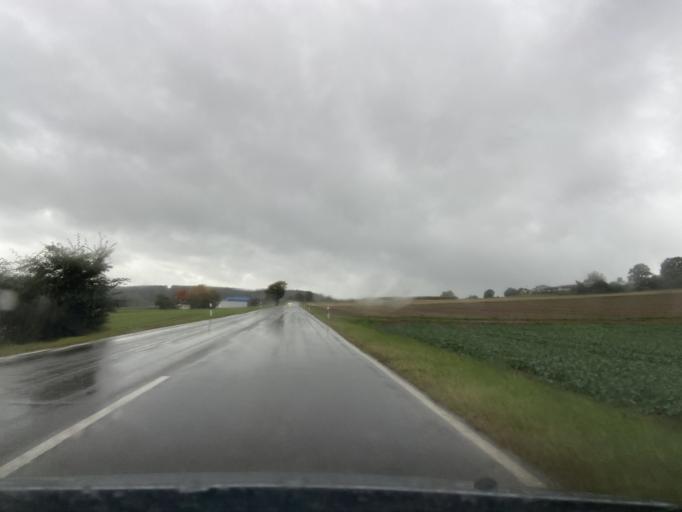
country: DE
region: Baden-Wuerttemberg
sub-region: Tuebingen Region
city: Scheer
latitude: 48.0710
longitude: 9.2829
